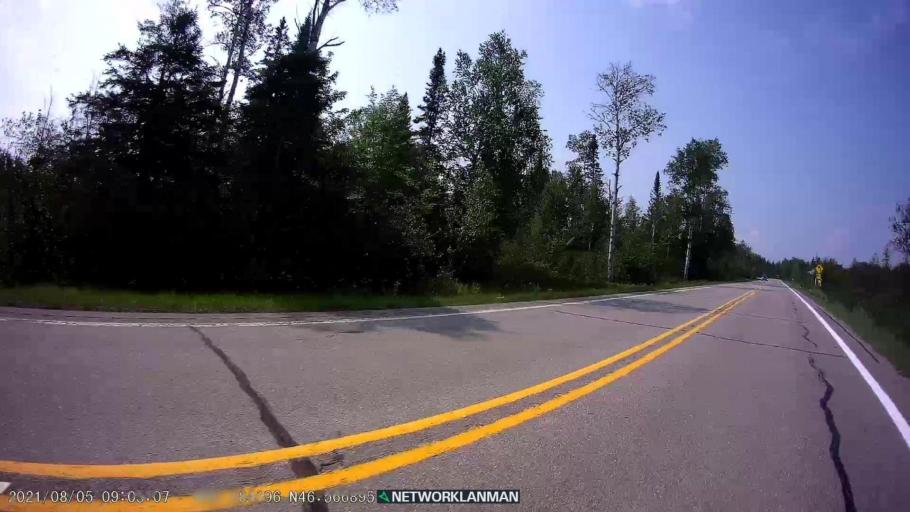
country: US
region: Michigan
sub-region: Luce County
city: Newberry
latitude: 46.5668
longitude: -85.2845
